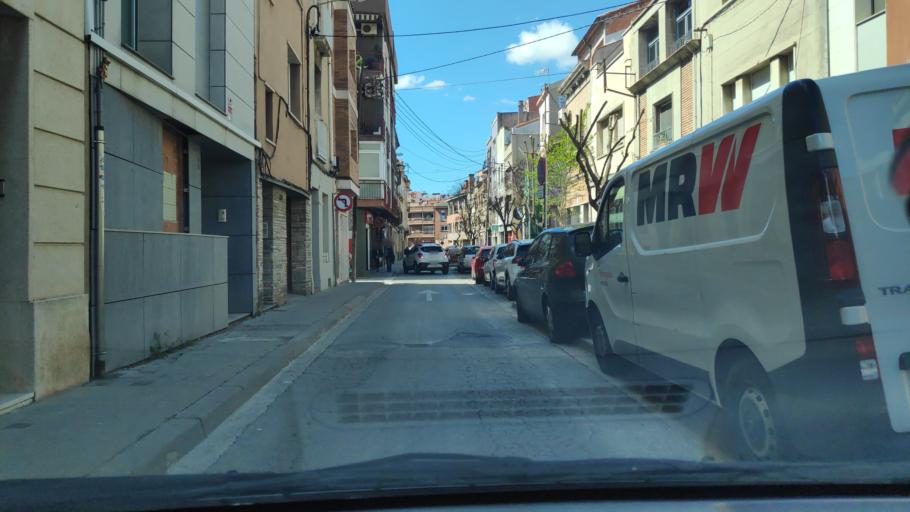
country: ES
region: Catalonia
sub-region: Provincia de Barcelona
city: Sabadell
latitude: 41.5509
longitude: 2.1103
